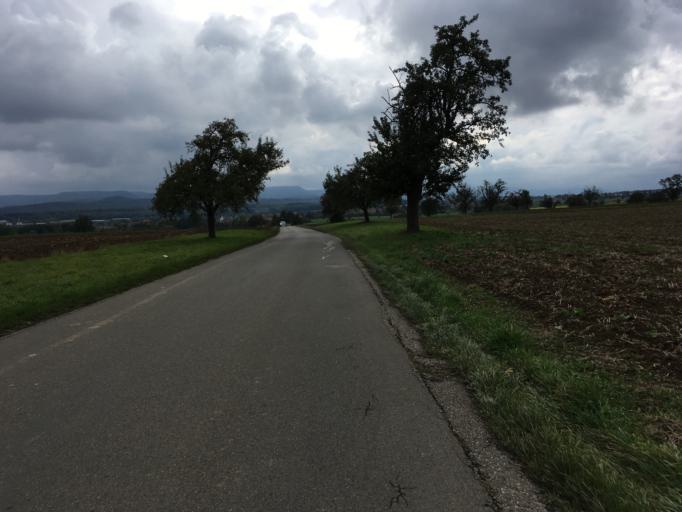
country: DE
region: Baden-Wuerttemberg
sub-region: Tuebingen Region
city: Kusterdingen
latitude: 48.5143
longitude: 9.1241
